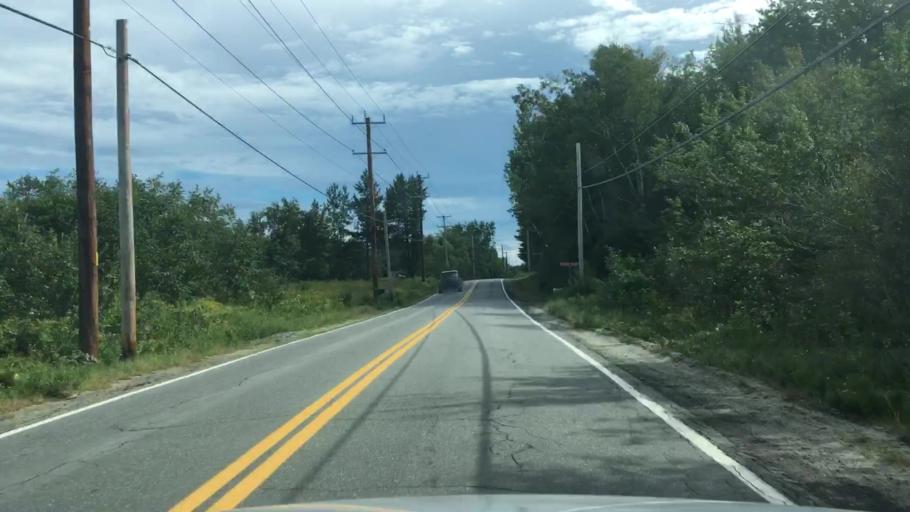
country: US
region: Maine
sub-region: Hancock County
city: Ellsworth
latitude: 44.4896
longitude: -68.4201
